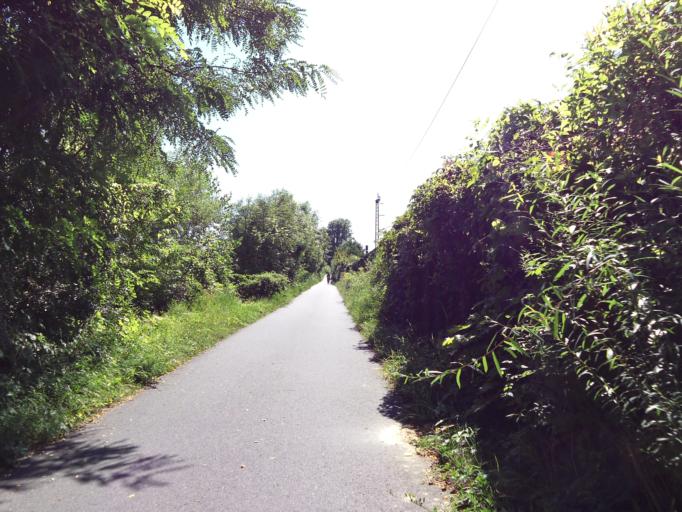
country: DE
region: Rheinland-Pfalz
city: Mainz
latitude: 49.9878
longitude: 8.2964
